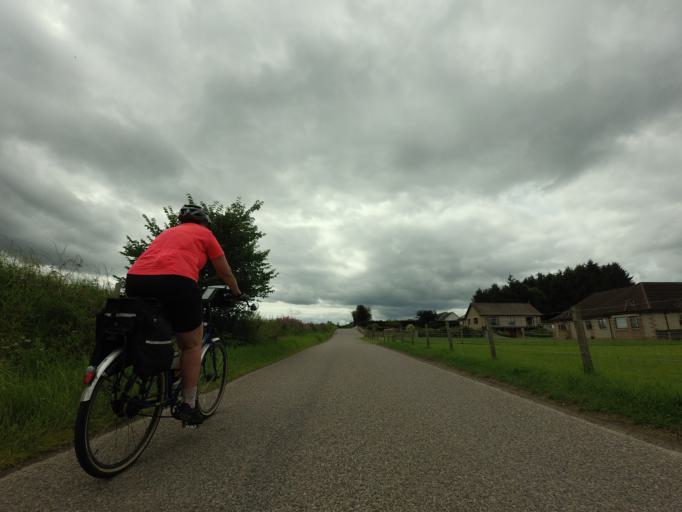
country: GB
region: Scotland
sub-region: Moray
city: Forres
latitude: 57.6005
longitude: -3.6956
